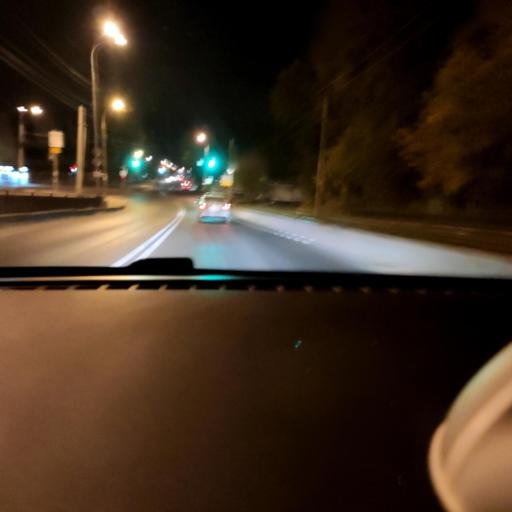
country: RU
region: Samara
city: Smyshlyayevka
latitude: 53.2164
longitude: 50.2913
